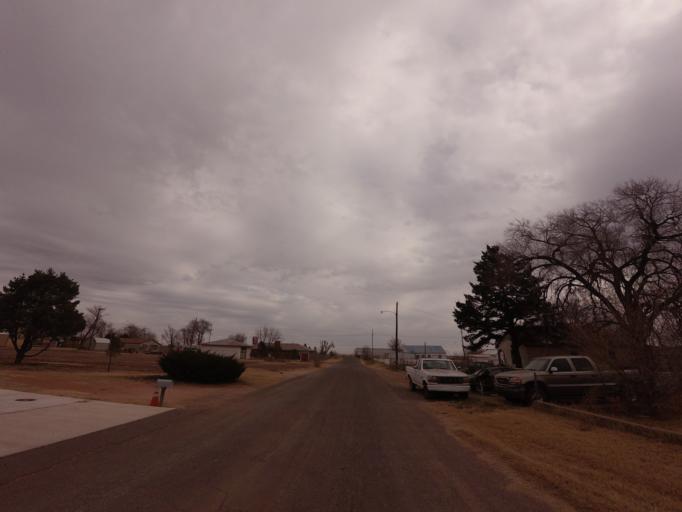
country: US
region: New Mexico
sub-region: Curry County
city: Clovis
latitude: 34.3775
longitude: -103.1980
